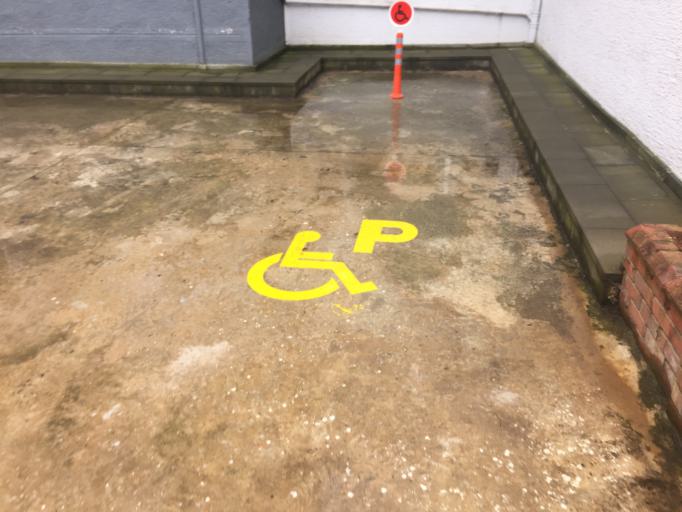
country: TR
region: Trabzon
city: Trabzon
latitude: 40.9919
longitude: 39.7749
